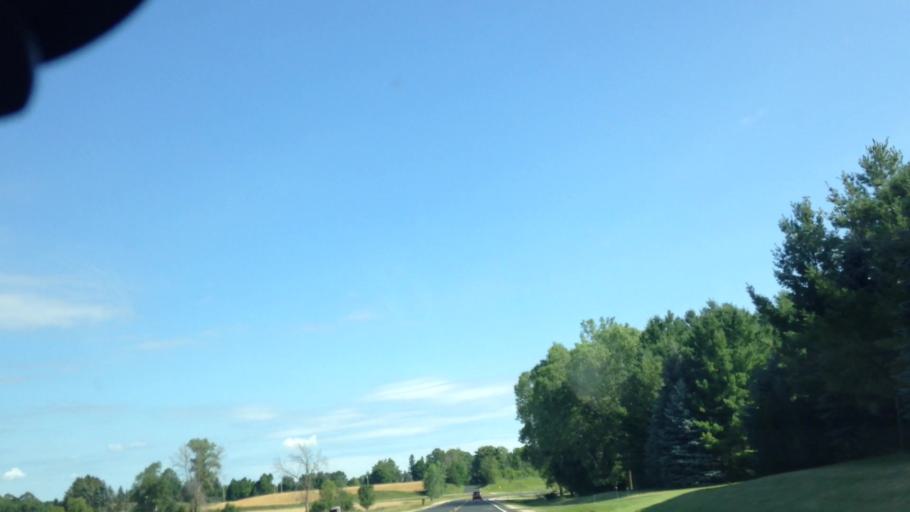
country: US
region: Wisconsin
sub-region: Washington County
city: Slinger
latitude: 43.3613
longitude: -88.2609
